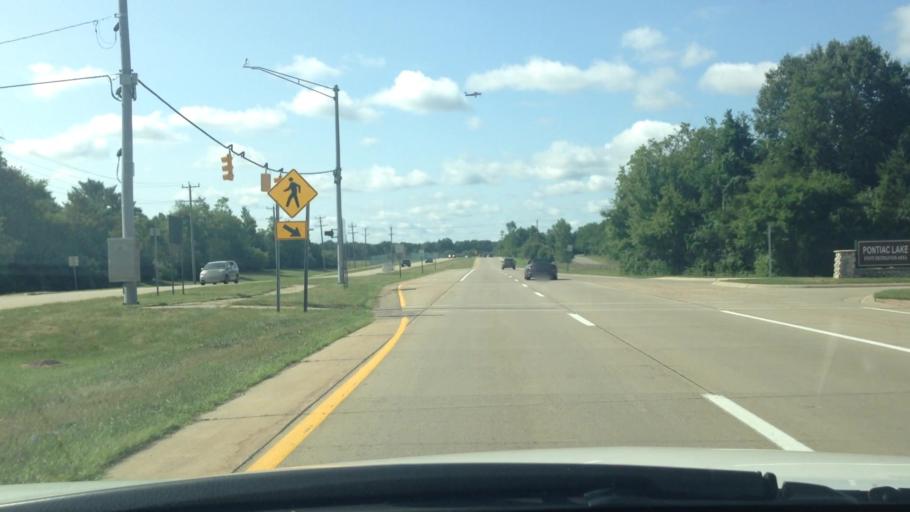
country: US
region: Michigan
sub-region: Oakland County
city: Waterford
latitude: 42.6697
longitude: -83.4388
